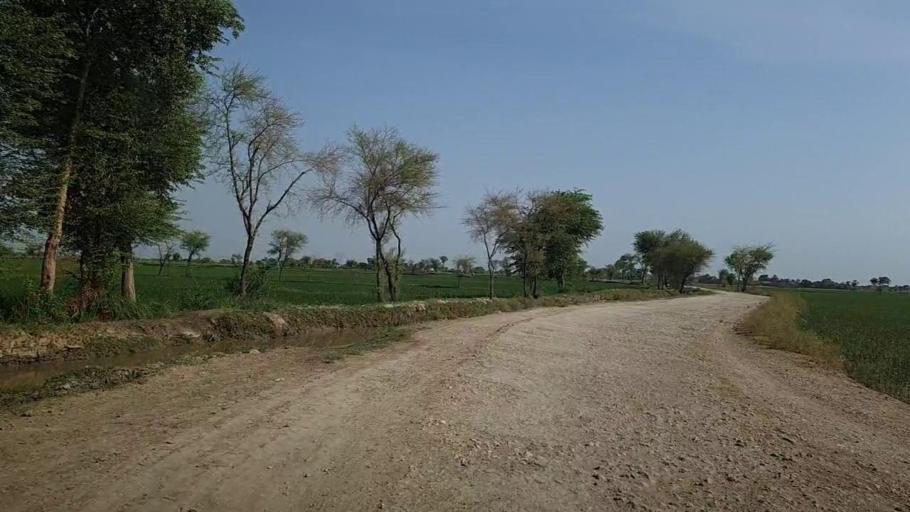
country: PK
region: Sindh
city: Sita Road
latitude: 27.1015
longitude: 67.8526
